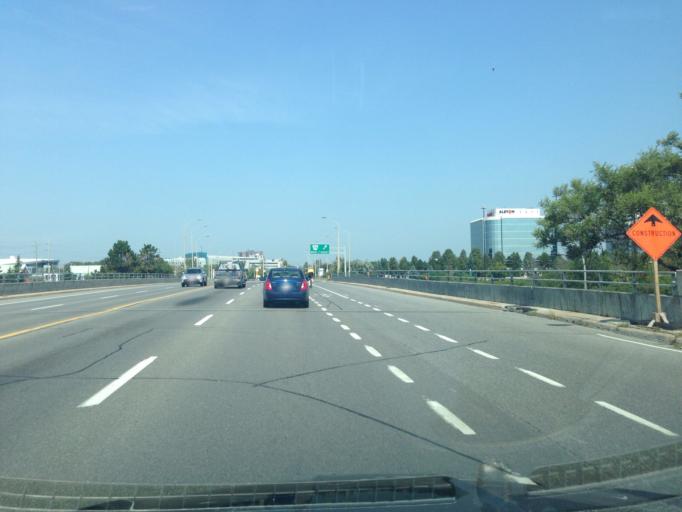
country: CA
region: Ontario
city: Ottawa
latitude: 45.4312
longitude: -75.6050
